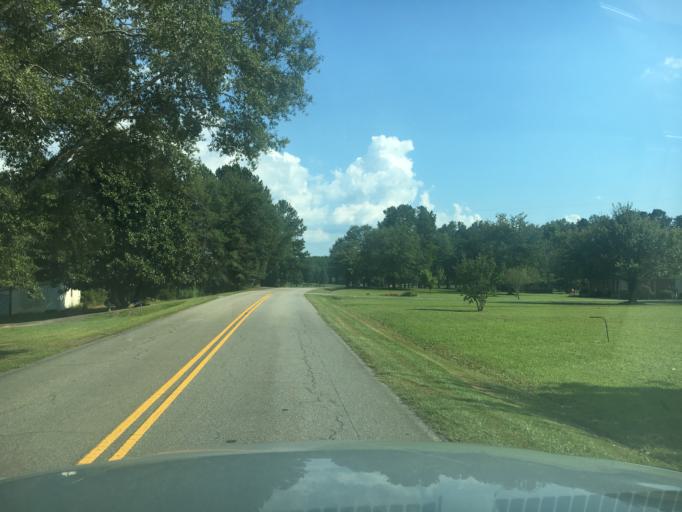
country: US
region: South Carolina
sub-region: Pickens County
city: Liberty
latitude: 34.7415
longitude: -82.6495
